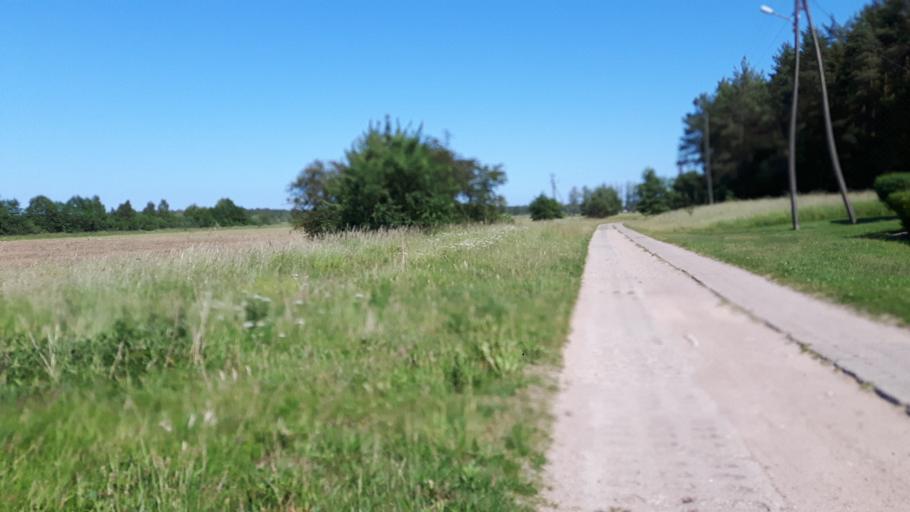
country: PL
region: Pomeranian Voivodeship
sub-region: Powiat slupski
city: Glowczyce
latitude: 54.6422
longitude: 17.3958
